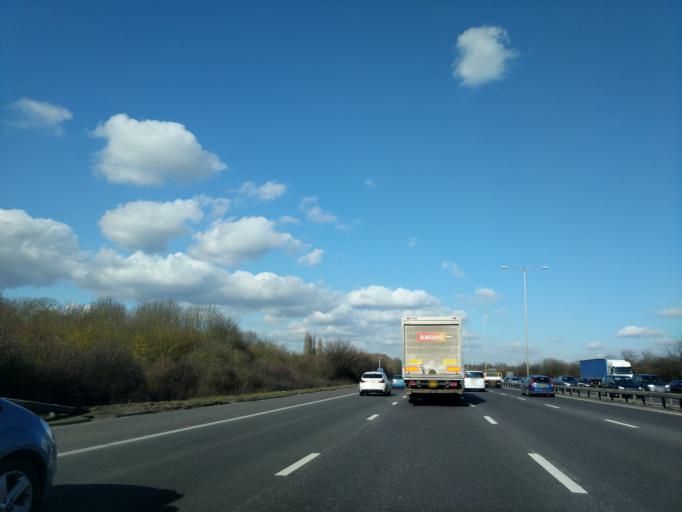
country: GB
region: England
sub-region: Buckinghamshire
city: Iver
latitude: 51.5250
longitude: -0.4986
